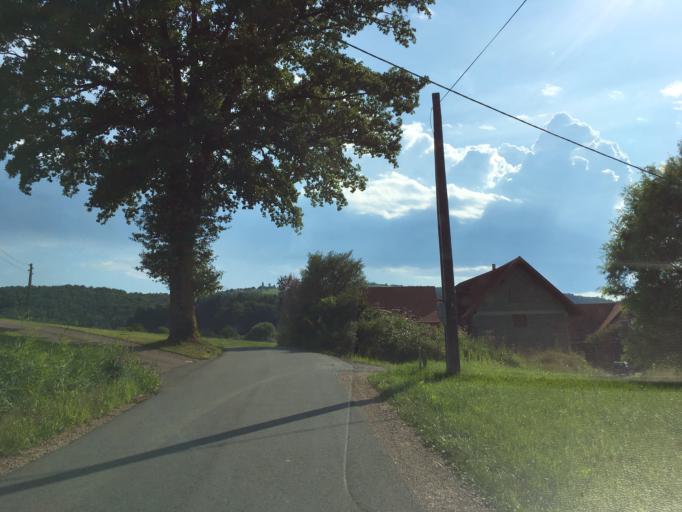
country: AT
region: Styria
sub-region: Politischer Bezirk Leibnitz
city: Sankt Nikolai im Sausal
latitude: 46.8157
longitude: 15.4583
